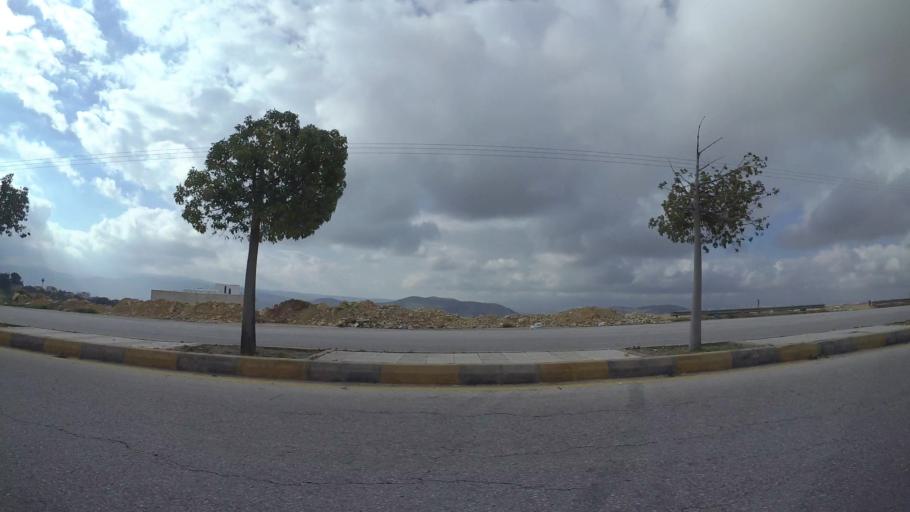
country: JO
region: Amman
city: Al Jubayhah
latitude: 32.0698
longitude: 35.8746
